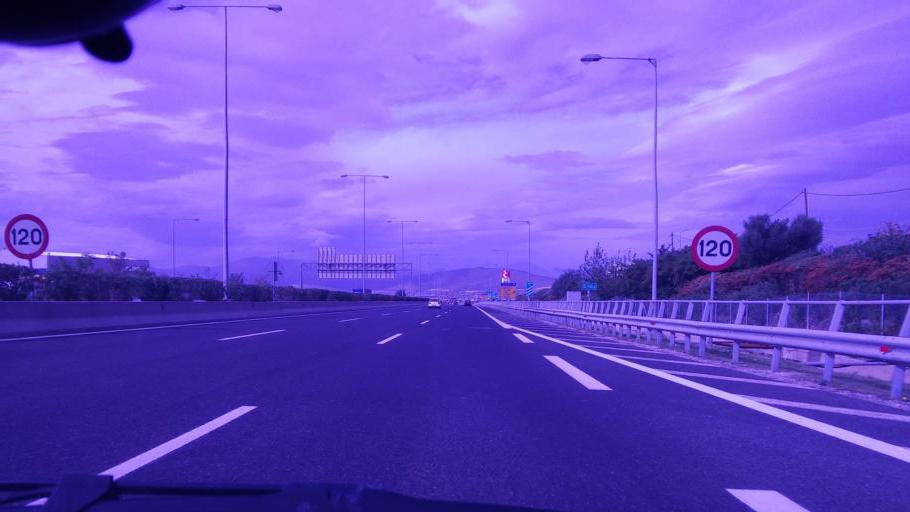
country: GR
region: Attica
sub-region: Nomarchia Dytikis Attikis
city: Aspropyrgos
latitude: 38.0913
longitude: 23.6136
